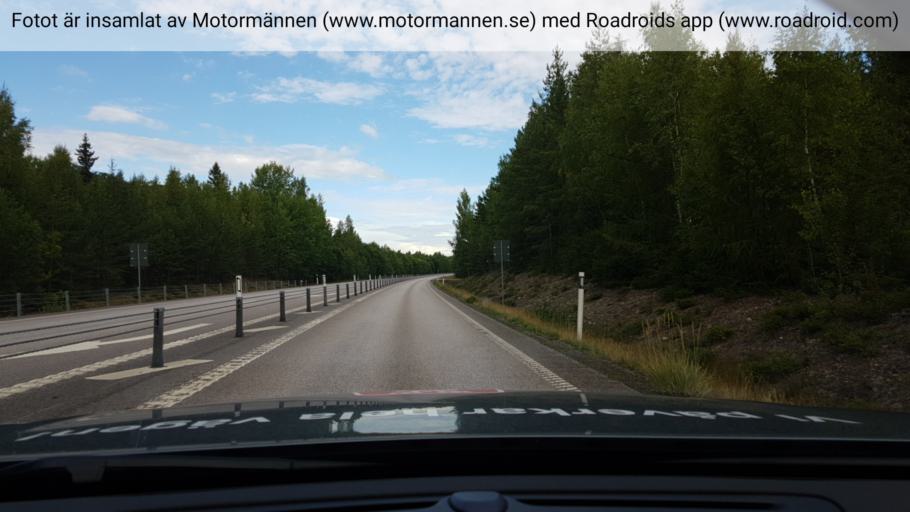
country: SE
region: Uppsala
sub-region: Heby Kommun
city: Tarnsjo
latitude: 60.2730
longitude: 16.9345
